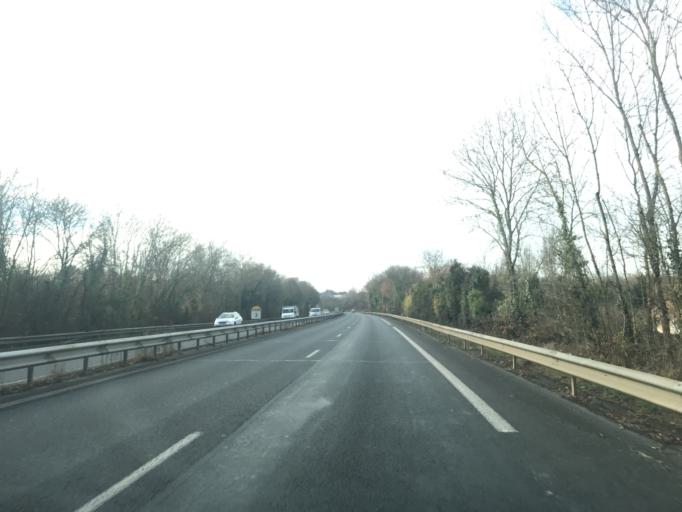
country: FR
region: Poitou-Charentes
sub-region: Departement des Deux-Sevres
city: Niort
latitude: 46.3353
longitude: -0.4409
